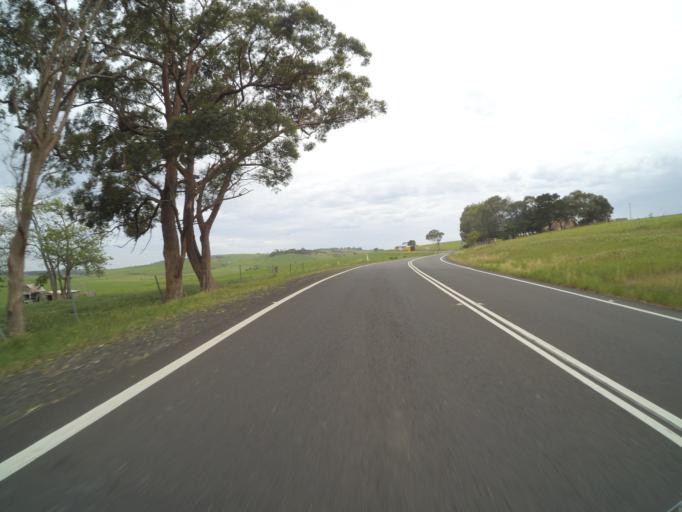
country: AU
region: New South Wales
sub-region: Kiama
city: Jamberoo
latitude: -34.6528
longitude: 150.8126
